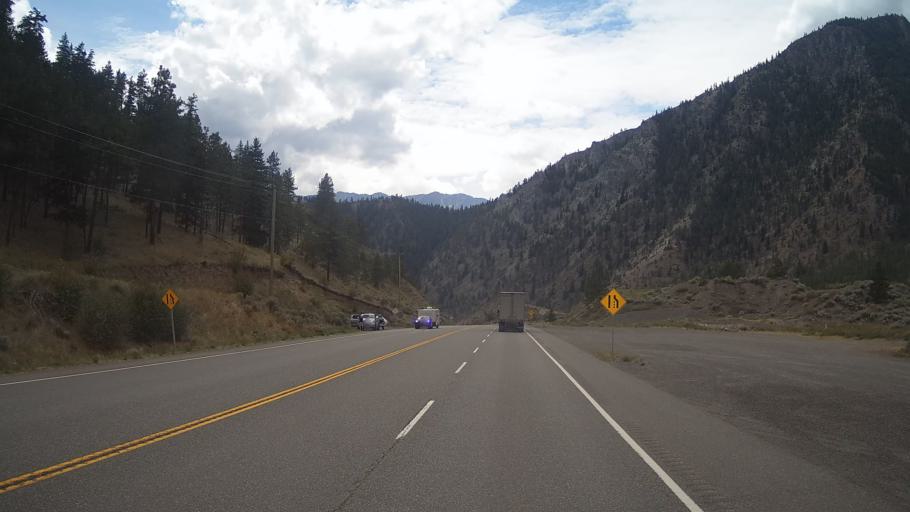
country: CA
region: British Columbia
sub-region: Thompson-Nicola Regional District
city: Ashcroft
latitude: 50.2878
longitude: -121.3992
